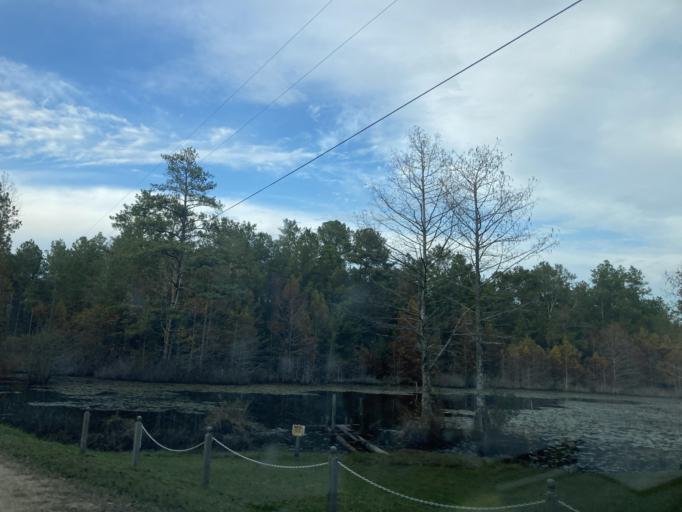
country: US
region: Mississippi
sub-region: Lamar County
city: Purvis
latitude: 31.1815
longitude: -89.3539
